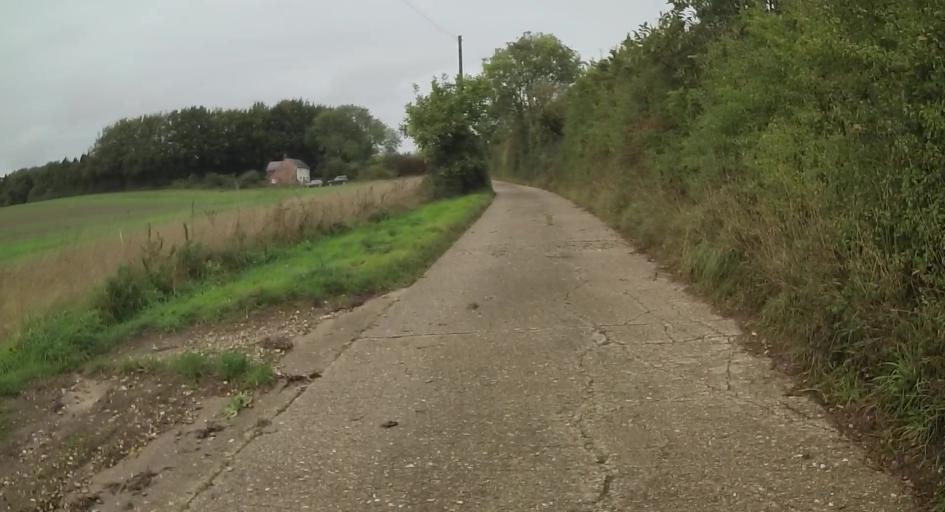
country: GB
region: England
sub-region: Hampshire
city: Basingstoke
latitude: 51.2709
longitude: -1.1339
